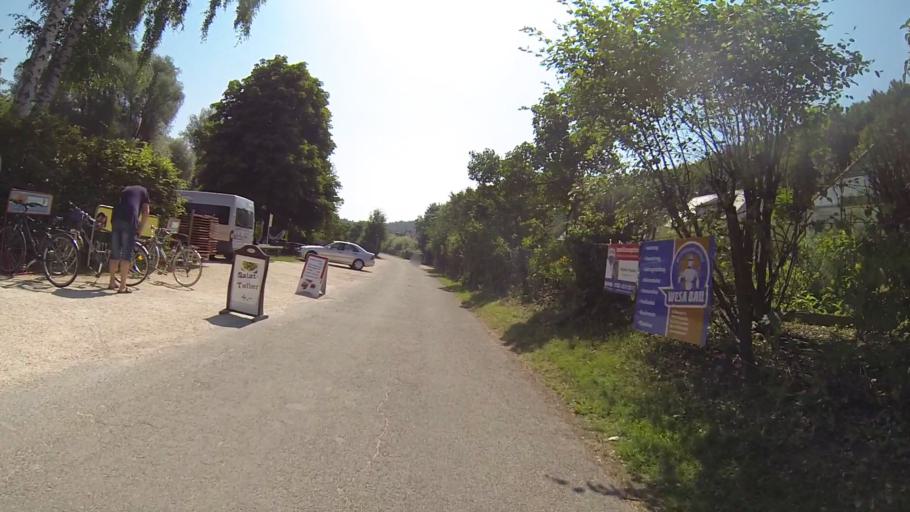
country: DE
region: Baden-Wuerttemberg
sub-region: Regierungsbezirk Stuttgart
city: Konigsbronn
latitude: 48.7320
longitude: 10.1309
